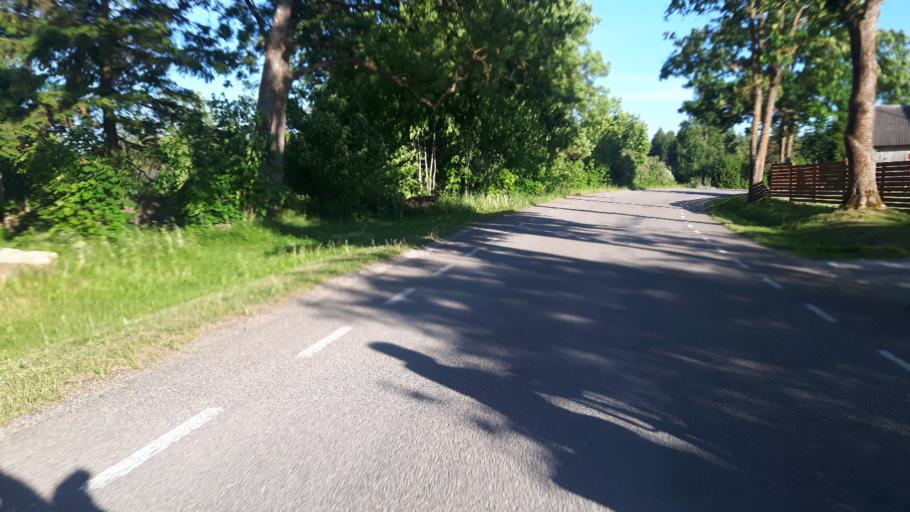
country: EE
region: Raplamaa
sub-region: Kehtna vald
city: Kehtna
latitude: 58.8988
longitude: 24.8794
